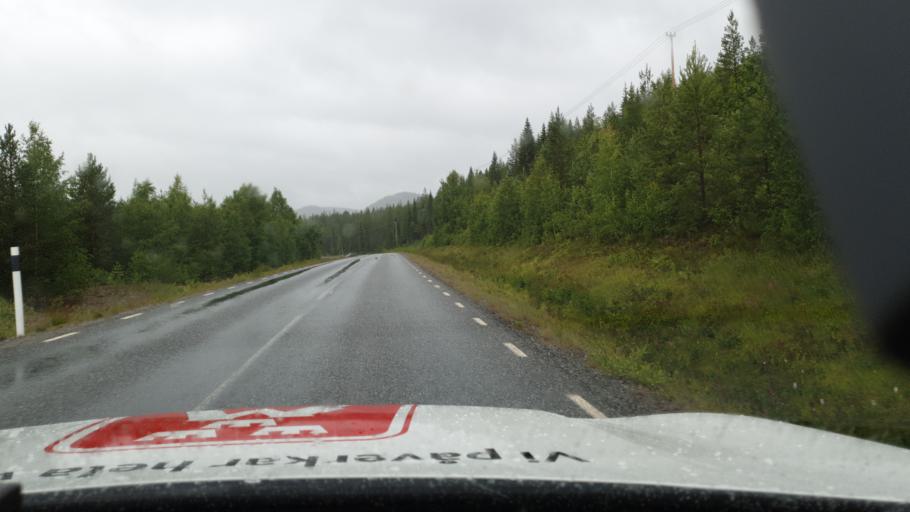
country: SE
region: Vaesterbotten
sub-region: Asele Kommun
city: Asele
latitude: 64.3168
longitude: 17.2137
